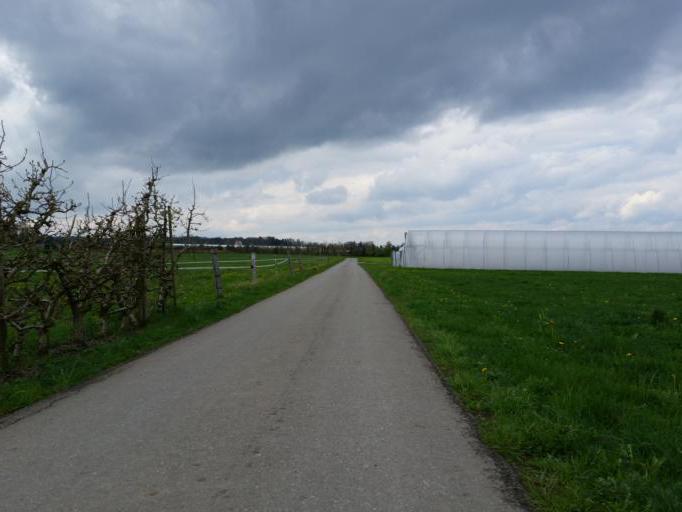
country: CH
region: Thurgau
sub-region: Arbon District
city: Uttwil
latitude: 47.5811
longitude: 9.3304
